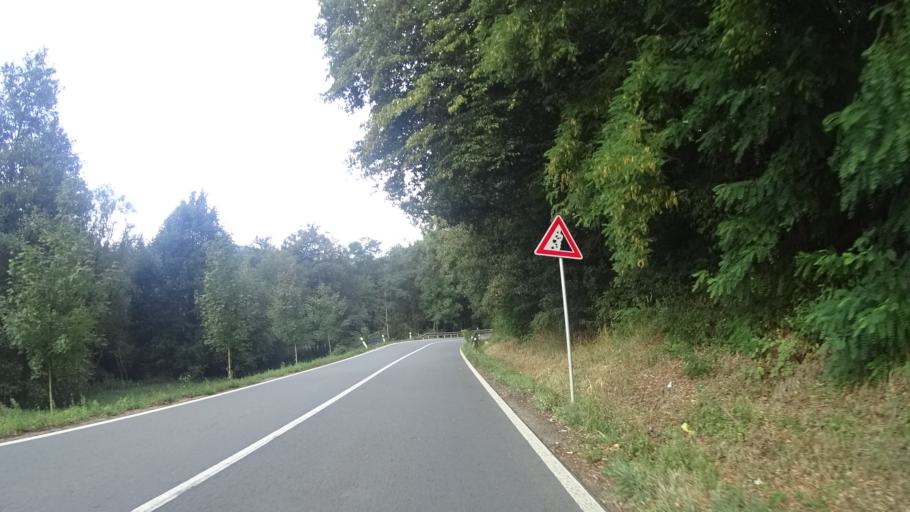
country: CZ
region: Olomoucky
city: Stity
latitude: 49.8648
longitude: 16.7398
